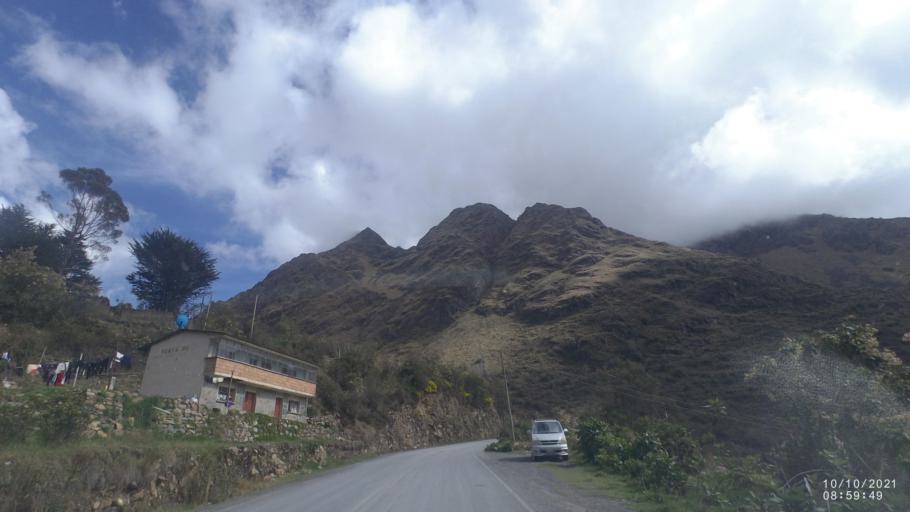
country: BO
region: La Paz
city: Quime
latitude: -16.9973
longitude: -67.2606
